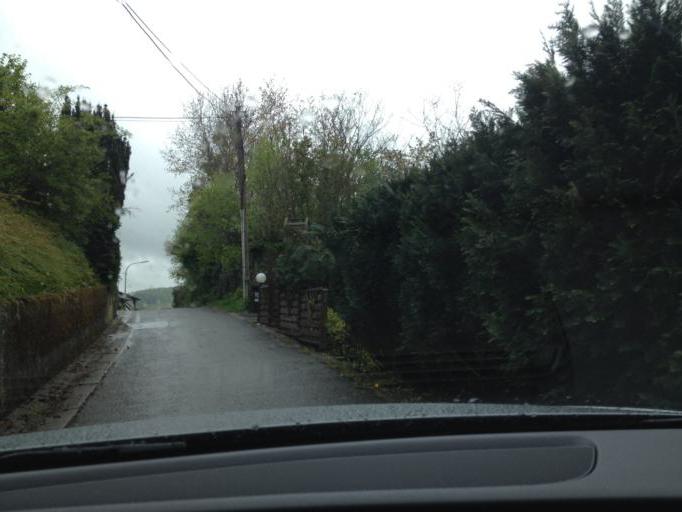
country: DE
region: Rheinland-Pfalz
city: Reichweiler
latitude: 49.5271
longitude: 7.2689
